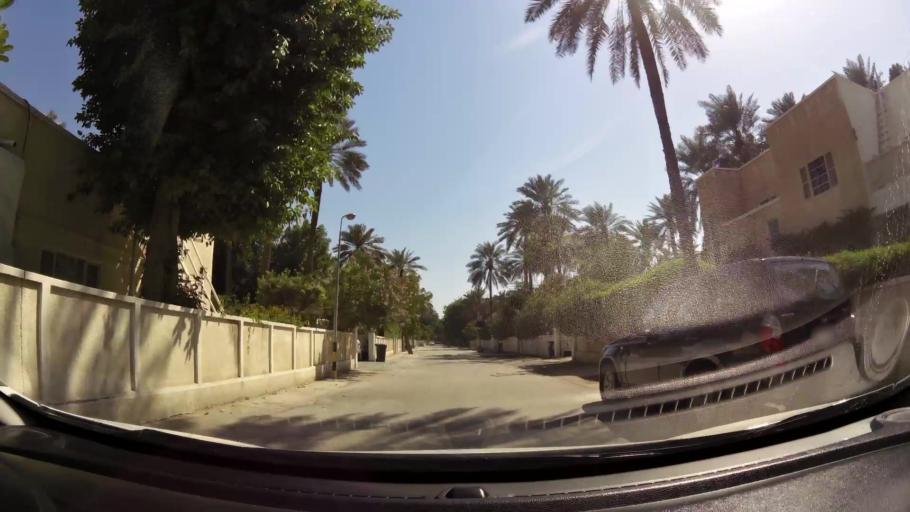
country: BH
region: Manama
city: Manama
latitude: 26.2169
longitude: 50.5822
